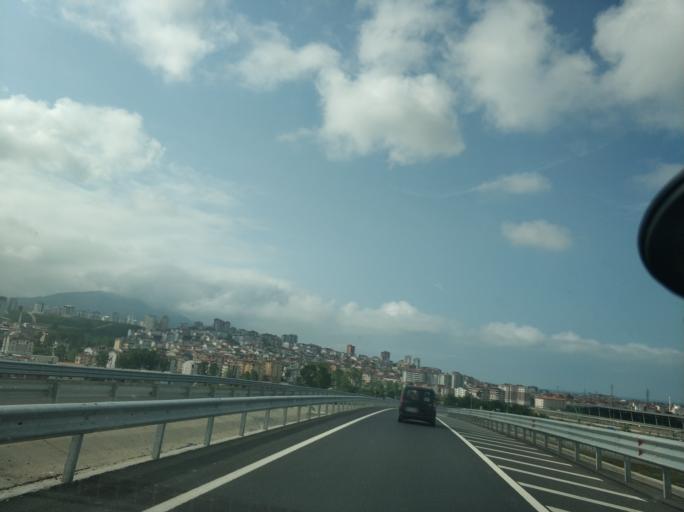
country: TR
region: Ordu
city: Ordu
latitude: 40.9539
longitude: 37.9028
